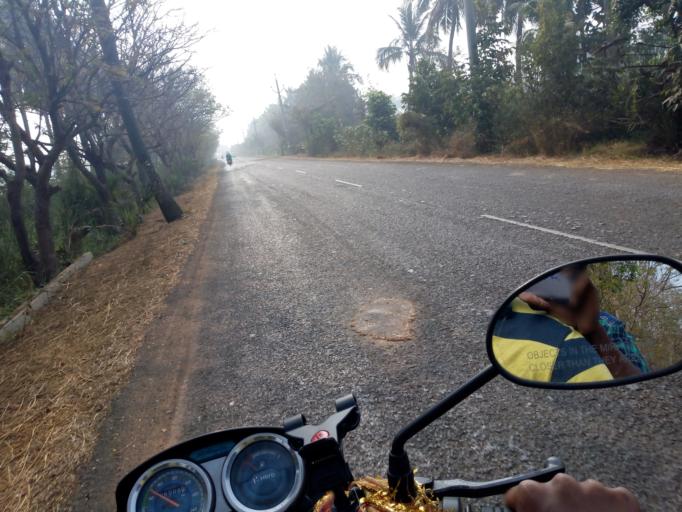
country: IN
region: Andhra Pradesh
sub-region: West Godavari
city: Tadepallegudem
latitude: 16.7945
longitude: 81.4164
